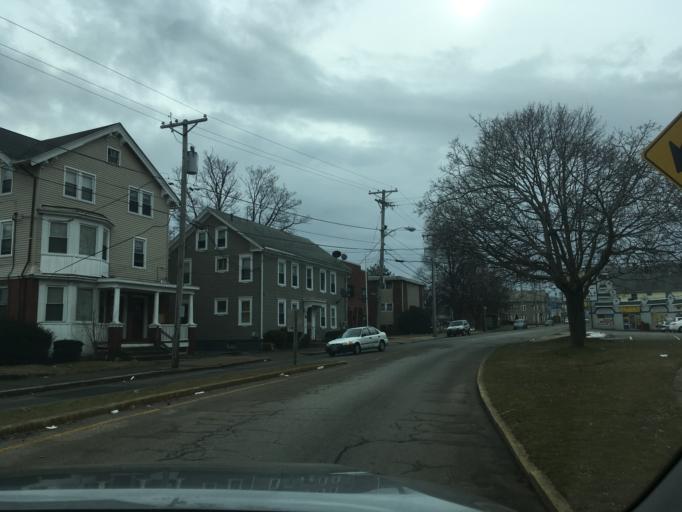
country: US
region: Rhode Island
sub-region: Providence County
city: Pawtucket
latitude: 41.8702
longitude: -71.3881
